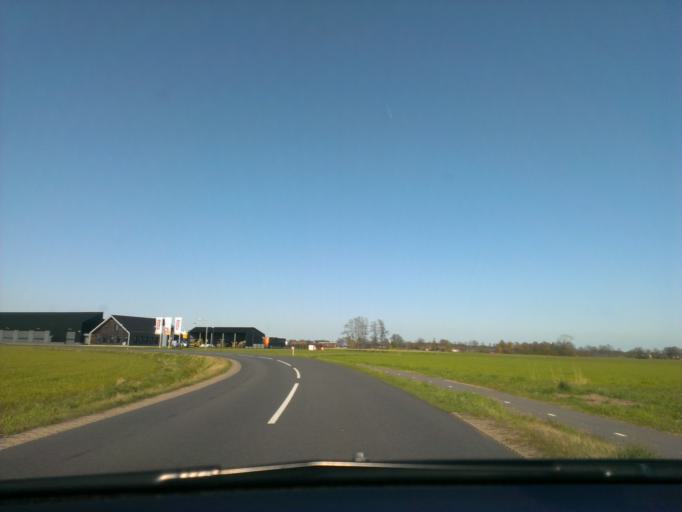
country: NL
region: Overijssel
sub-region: Gemeente Twenterand
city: Den Ham
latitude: 52.4545
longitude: 6.4878
